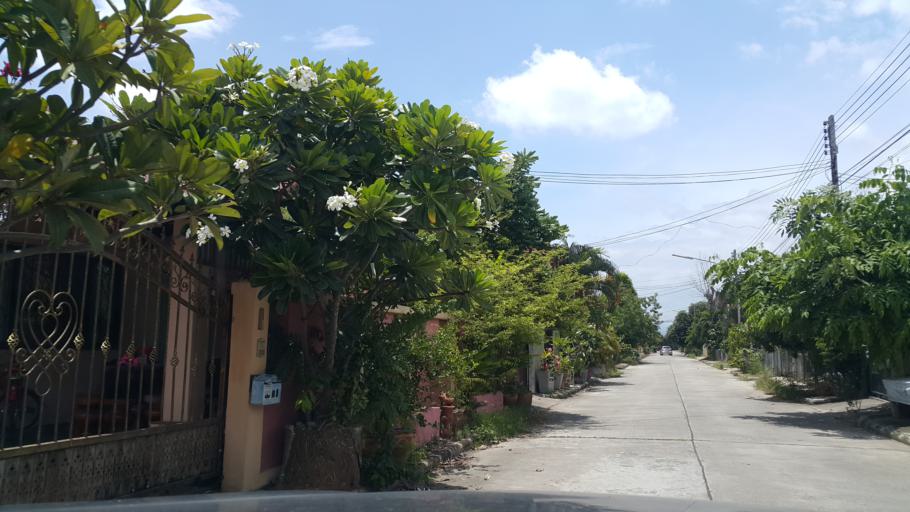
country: TH
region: Chiang Mai
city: Hang Dong
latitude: 18.7090
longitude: 98.9731
